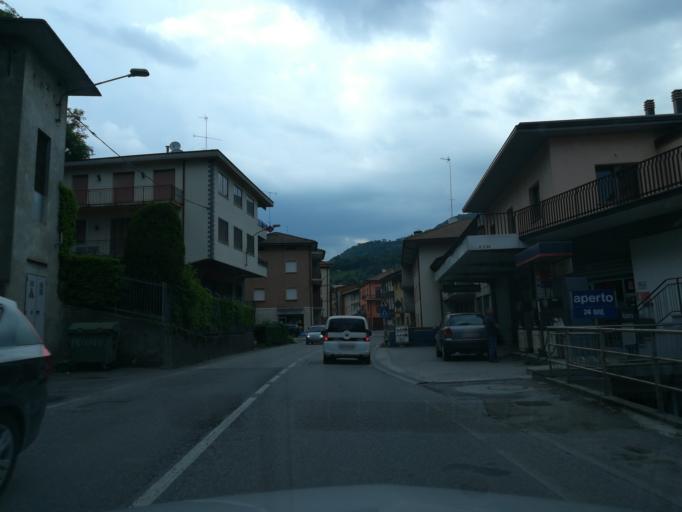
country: IT
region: Lombardy
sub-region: Provincia di Bergamo
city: Camoneone
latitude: 45.7834
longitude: 9.5736
